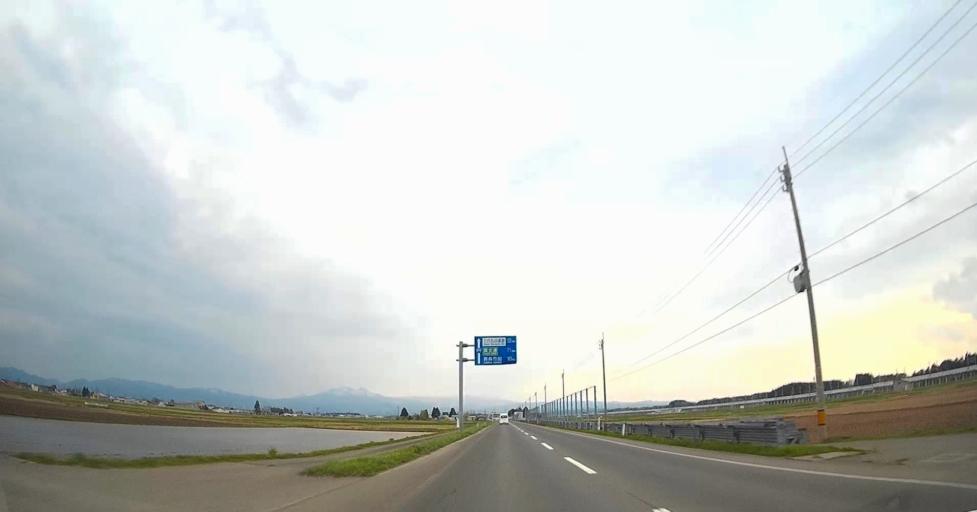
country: JP
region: Aomori
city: Aomori Shi
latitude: 40.8740
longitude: 140.6735
